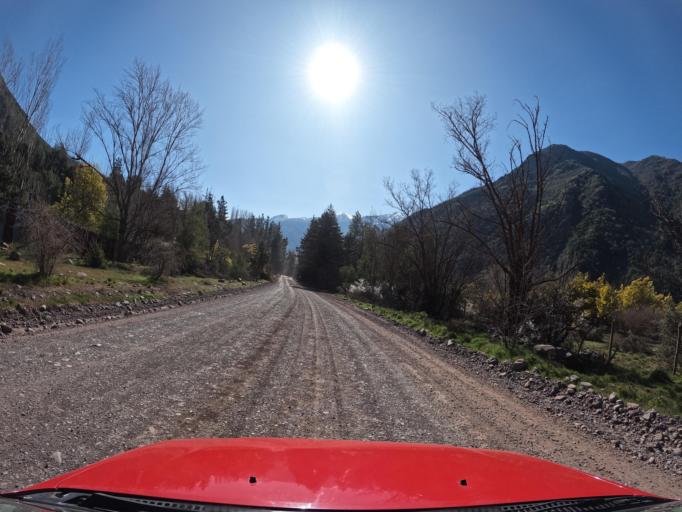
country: CL
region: O'Higgins
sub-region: Provincia de Colchagua
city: Chimbarongo
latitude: -35.0102
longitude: -70.7473
